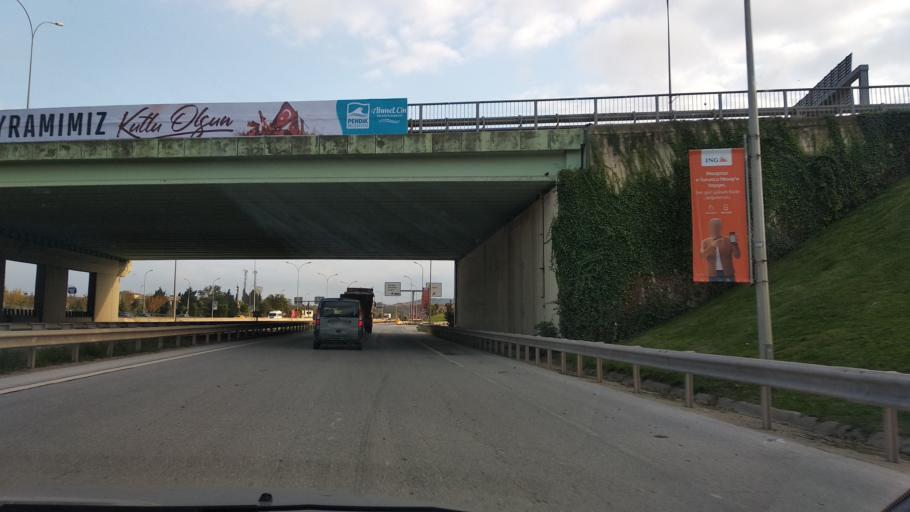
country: TR
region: Istanbul
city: Pendik
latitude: 40.9149
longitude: 29.3241
